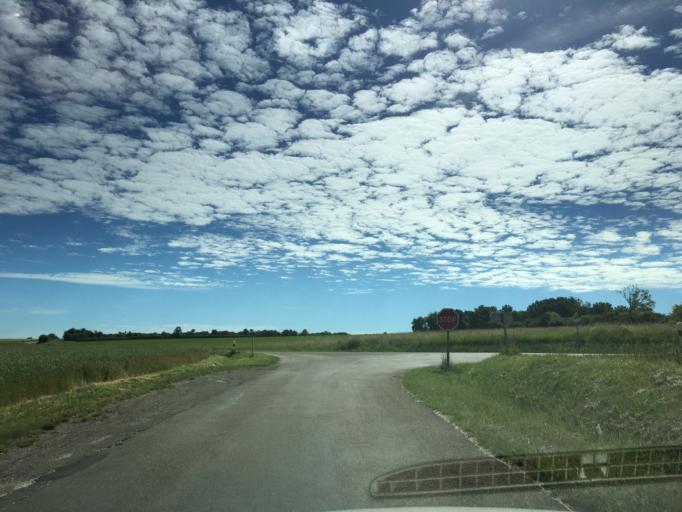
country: FR
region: Bourgogne
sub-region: Departement de l'Yonne
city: Saint-Georges-sur-Baulche
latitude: 47.7651
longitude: 3.5198
